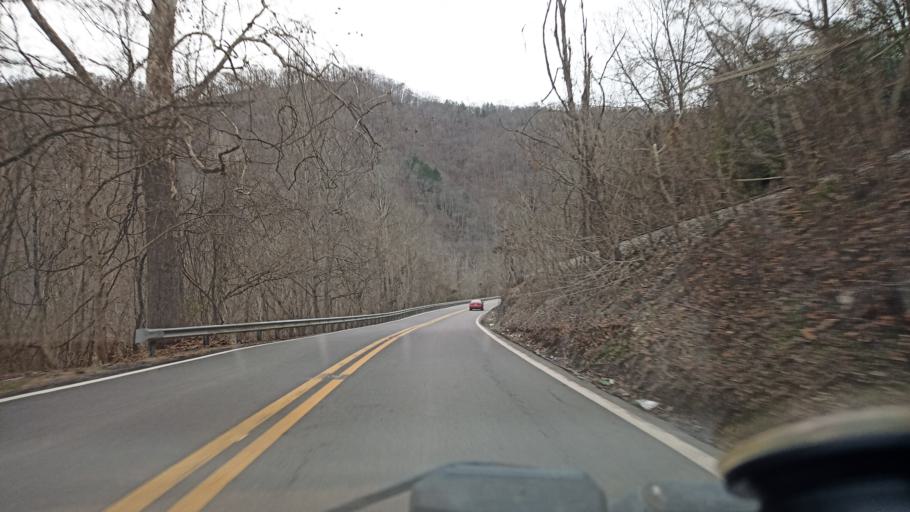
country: US
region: West Virginia
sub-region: Logan County
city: Mallory
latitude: 37.6926
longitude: -81.8676
